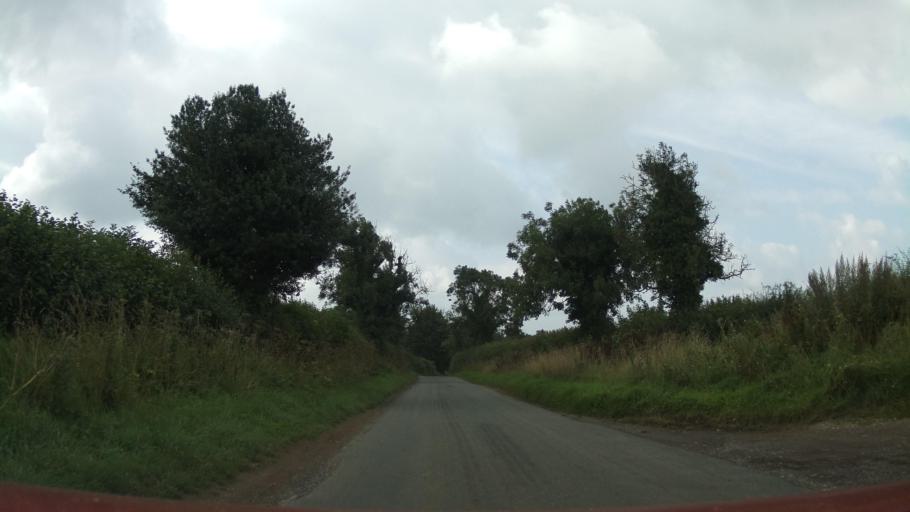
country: GB
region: England
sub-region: Somerset
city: Evercreech
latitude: 51.1826
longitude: -2.5063
